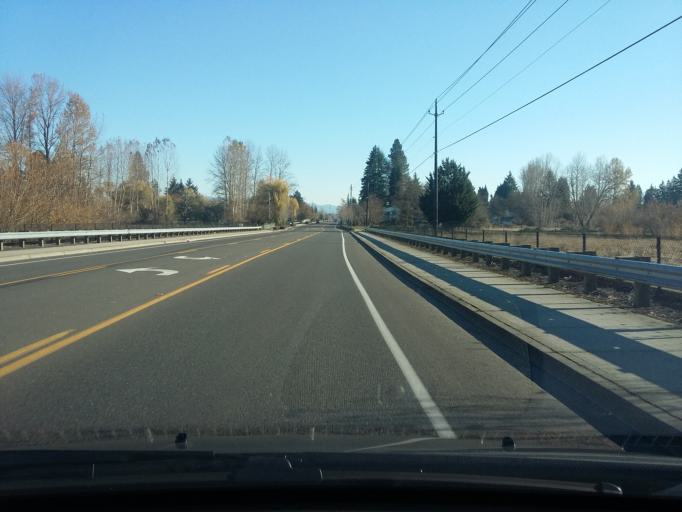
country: US
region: Washington
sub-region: Clark County
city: Barberton
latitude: 45.6859
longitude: -122.6235
